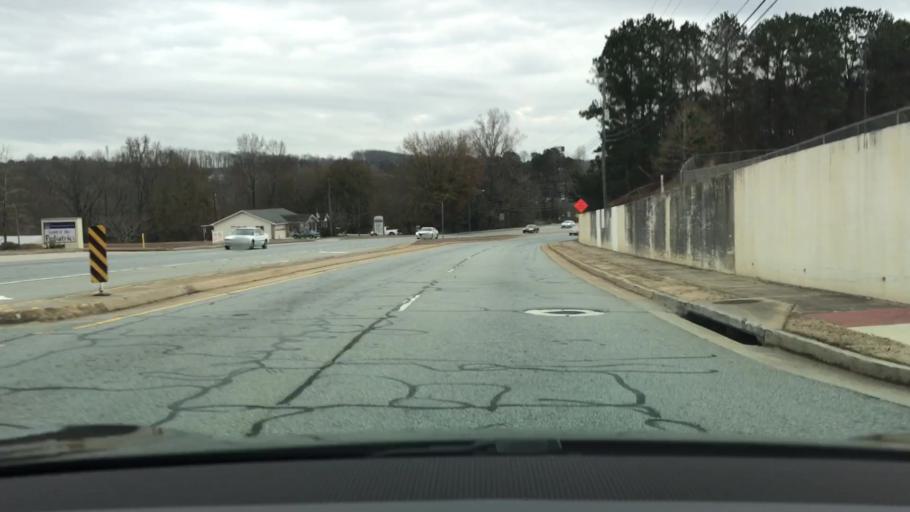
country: US
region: Georgia
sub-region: Gwinnett County
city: Buford
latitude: 34.0937
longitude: -83.9992
